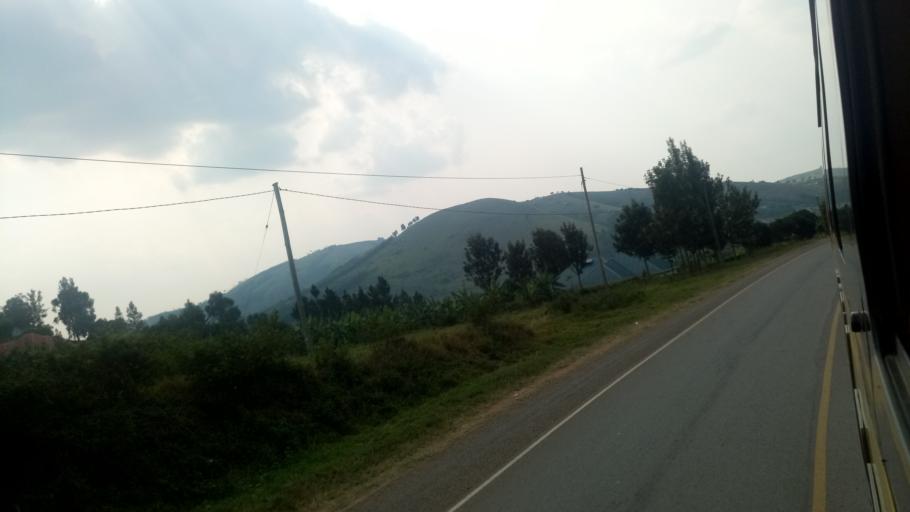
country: UG
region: Western Region
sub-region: Mbarara District
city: Mbarara
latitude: -0.5450
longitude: 30.7135
